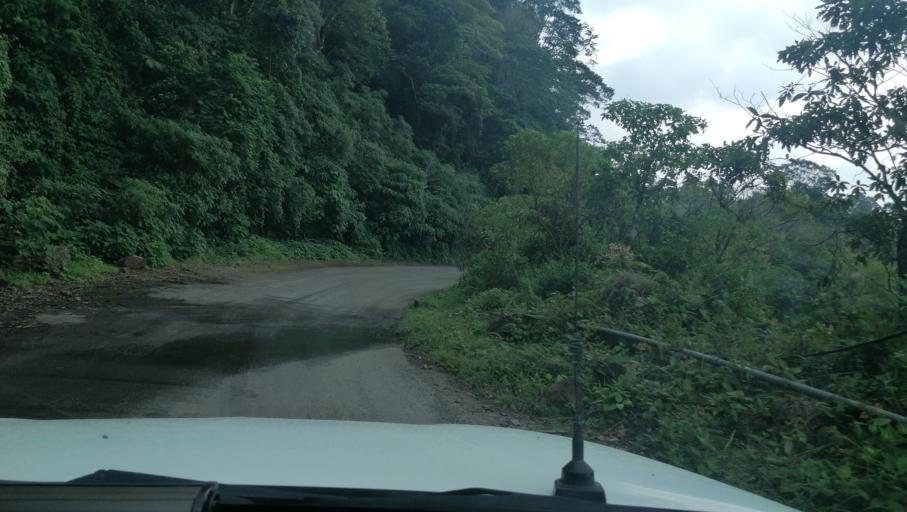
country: MX
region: Chiapas
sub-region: Francisco Leon
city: San Miguel la Sardina
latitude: 17.2431
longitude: -93.2927
